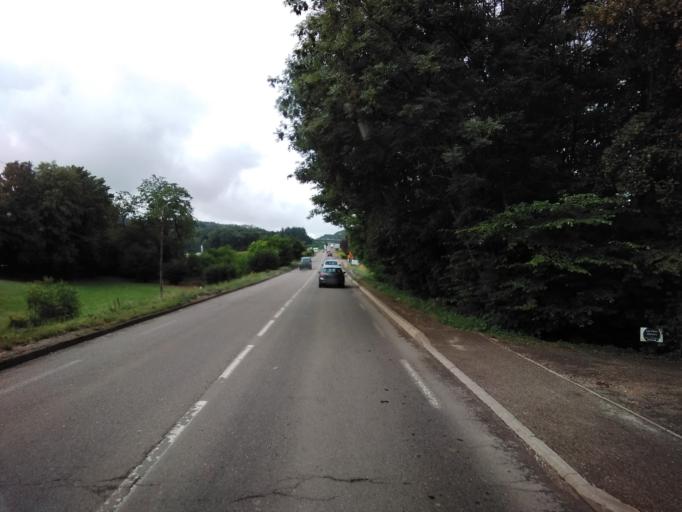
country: FR
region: Franche-Comte
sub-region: Departement du Doubs
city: Chatillon-le-Duc
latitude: 47.3140
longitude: 5.9952
